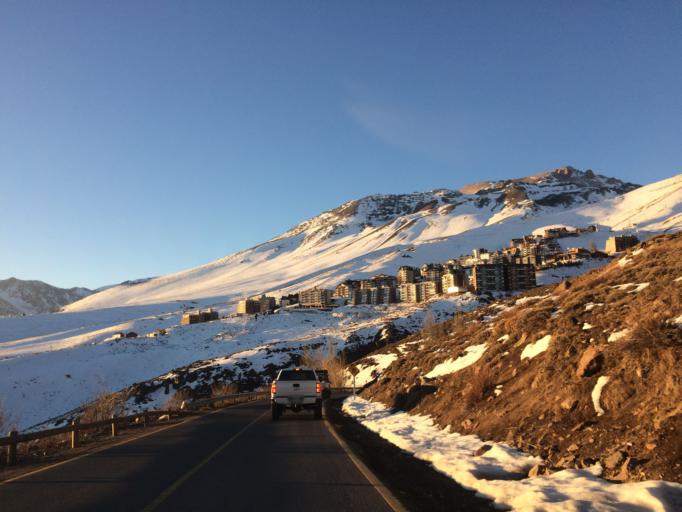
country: CL
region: Santiago Metropolitan
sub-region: Provincia de Santiago
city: Villa Presidente Frei, Nunoa, Santiago, Chile
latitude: -33.3417
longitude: -70.2945
